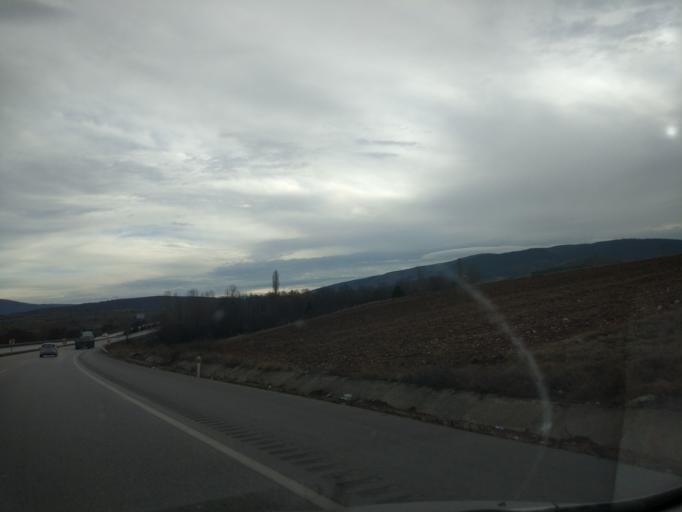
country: TR
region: Karabuk
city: Eskipazar
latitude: 40.9292
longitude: 32.5838
